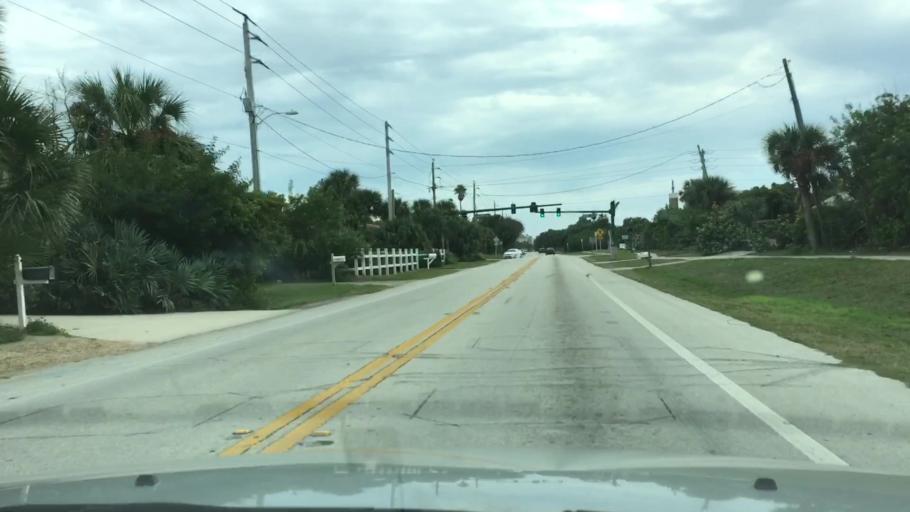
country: US
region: Florida
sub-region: Volusia County
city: Ormond Beach
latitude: 29.3021
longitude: -81.0450
